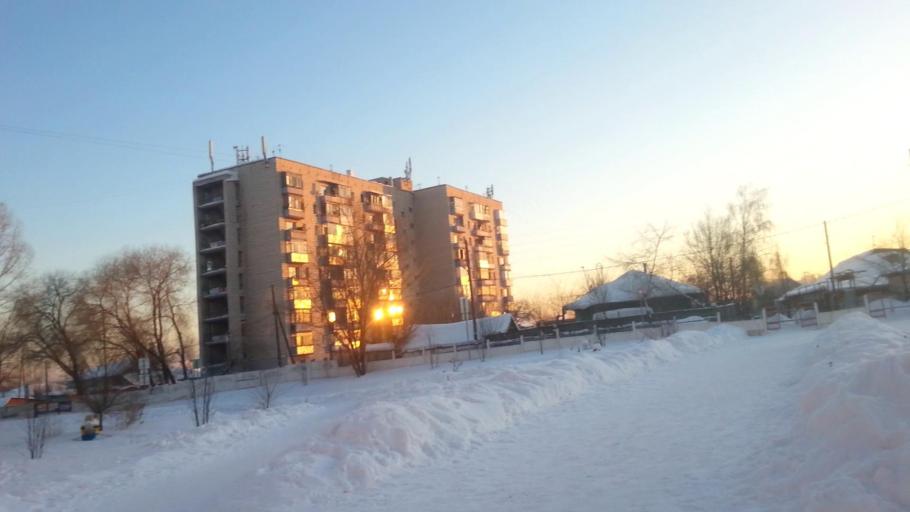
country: RU
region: Altai Krai
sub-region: Gorod Barnaulskiy
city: Barnaul
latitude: 53.3539
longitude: 83.7047
